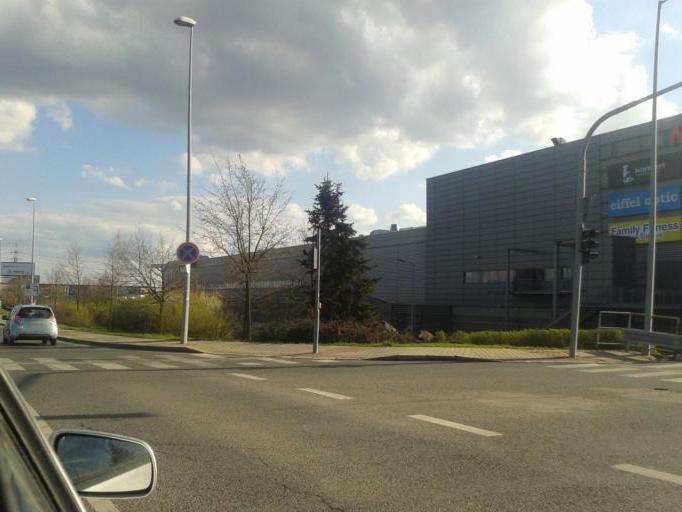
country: CZ
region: Central Bohemia
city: Hostivice
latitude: 50.0552
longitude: 14.2887
